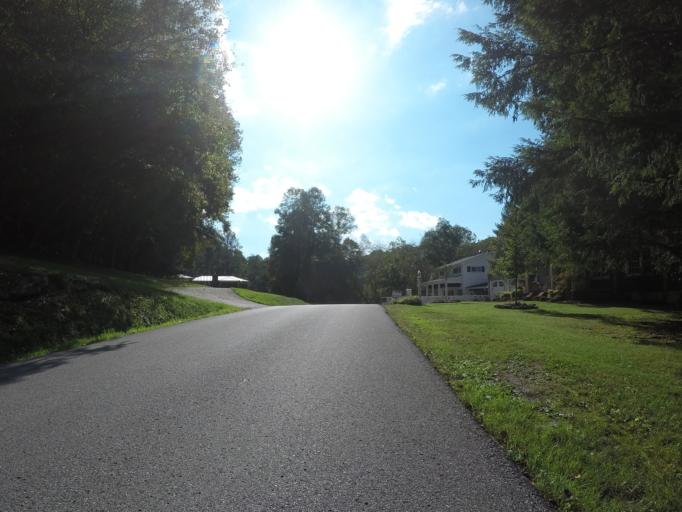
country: US
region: West Virginia
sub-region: Wayne County
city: Lavalette
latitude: 38.3600
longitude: -82.4846
